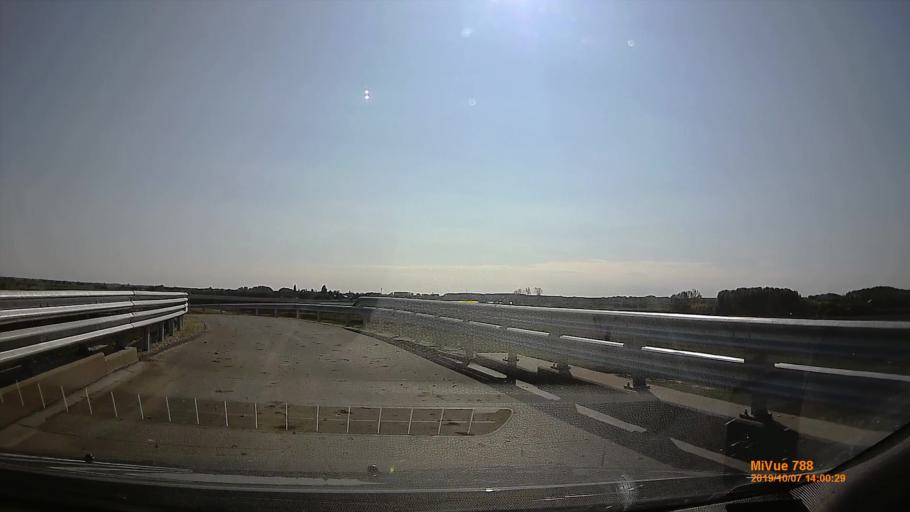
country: HU
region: Jasz-Nagykun-Szolnok
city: Cserkeszolo
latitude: 46.8843
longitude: 20.2119
